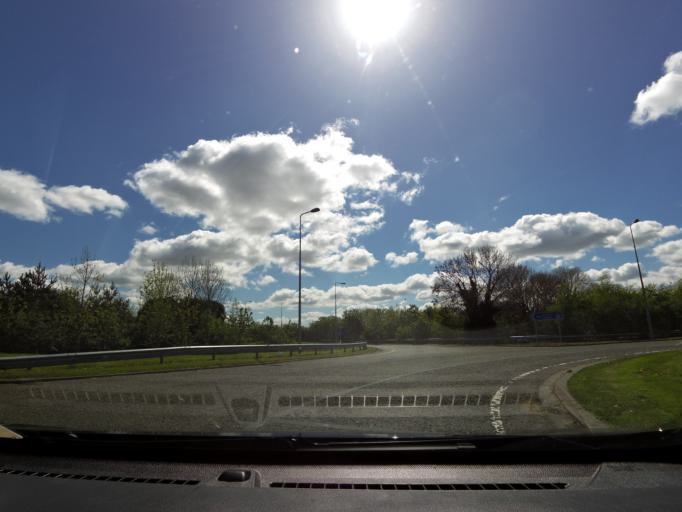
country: IE
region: Leinster
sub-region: An Mhi
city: Enfield
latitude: 53.4135
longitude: -6.8790
